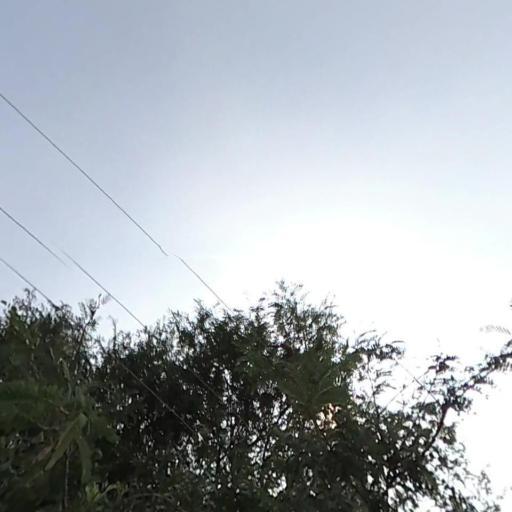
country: IN
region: Telangana
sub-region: Nalgonda
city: Nalgonda
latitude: 17.2077
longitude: 79.1562
